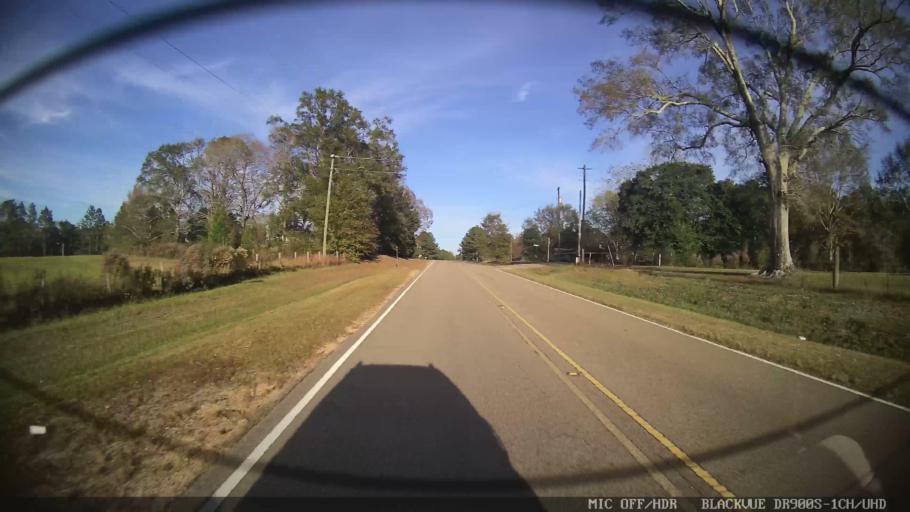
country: US
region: Mississippi
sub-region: Lamar County
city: Purvis
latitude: 31.1696
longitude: -89.3013
